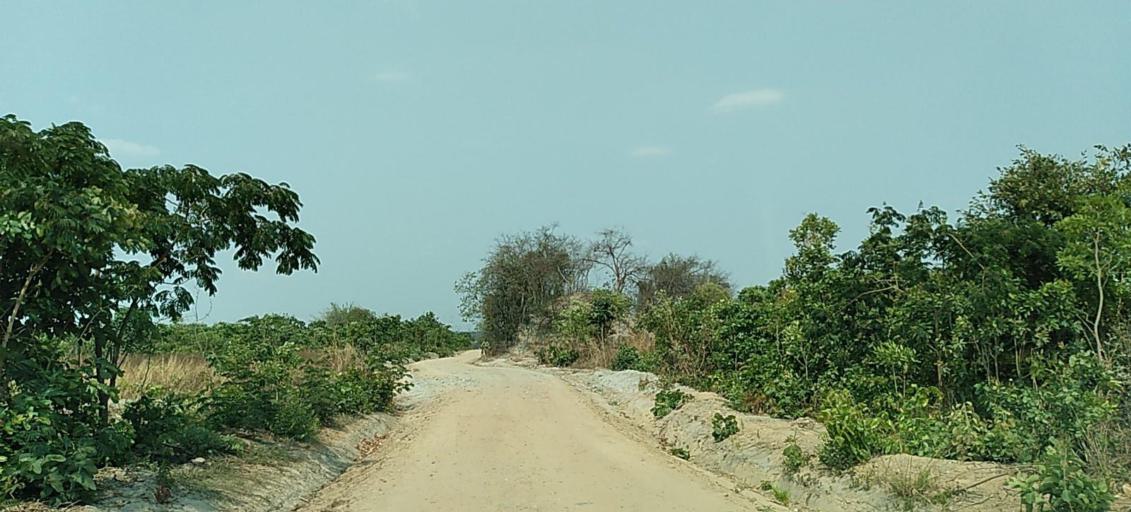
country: ZM
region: Copperbelt
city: Chambishi
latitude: -12.6221
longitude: 28.0868
